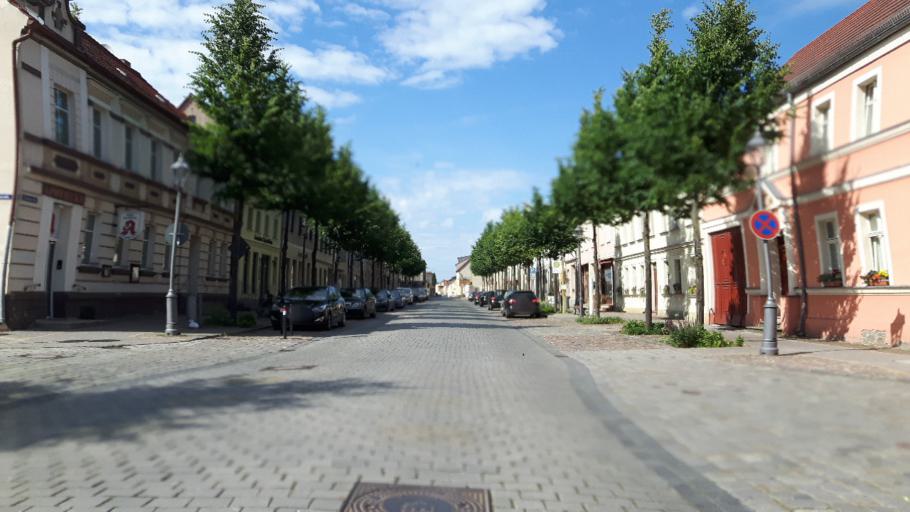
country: DE
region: Brandenburg
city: Beelitz
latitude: 52.2330
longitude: 12.9779
